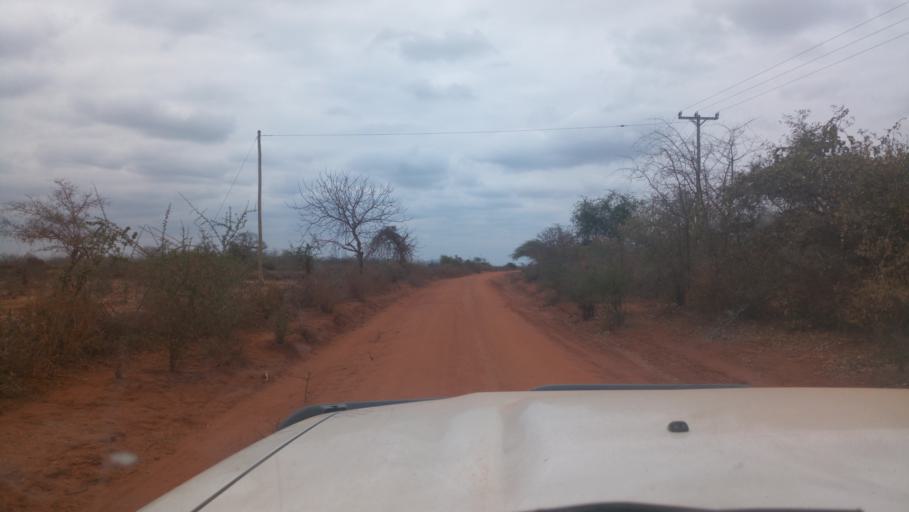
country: KE
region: Makueni
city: Wote
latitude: -1.8451
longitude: 38.0092
